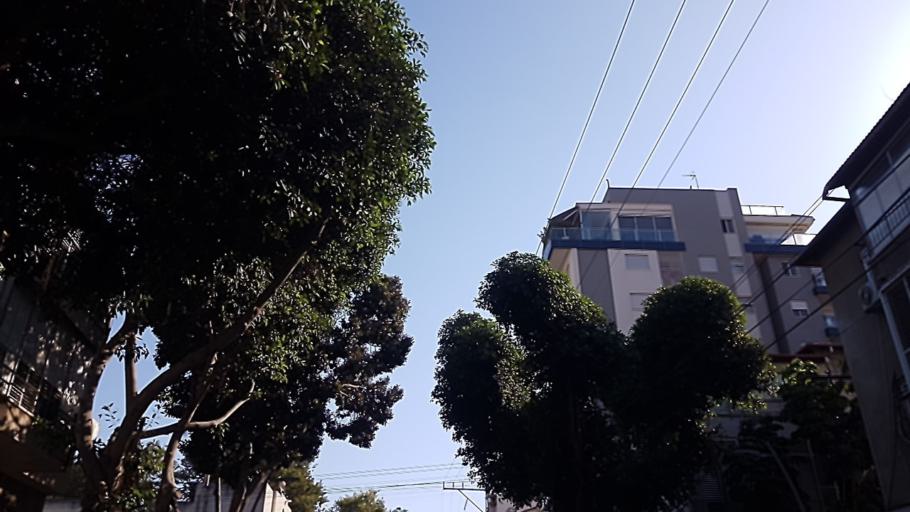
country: IL
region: Tel Aviv
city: Bene Beraq
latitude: 32.0788
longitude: 34.8233
